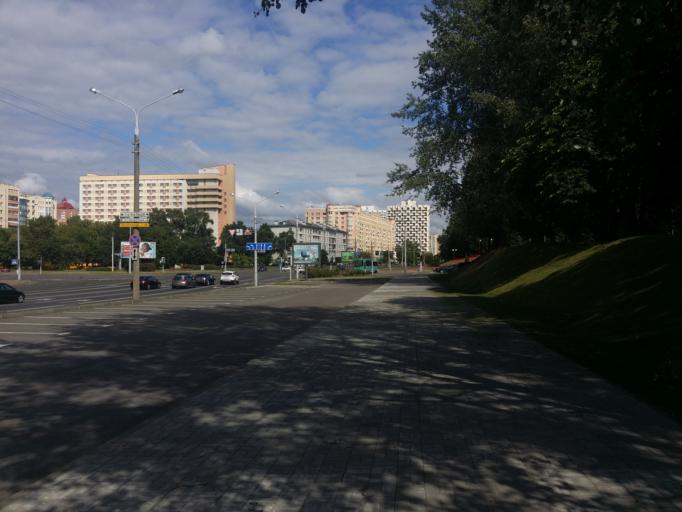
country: BY
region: Minsk
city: Minsk
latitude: 53.9175
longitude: 27.5512
